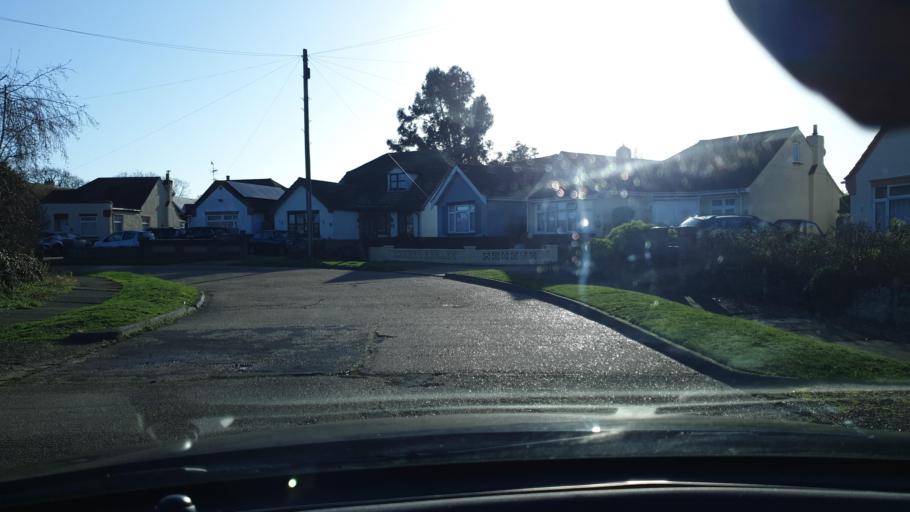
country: GB
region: England
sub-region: Essex
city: Clacton-on-Sea
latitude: 51.8068
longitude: 1.1893
